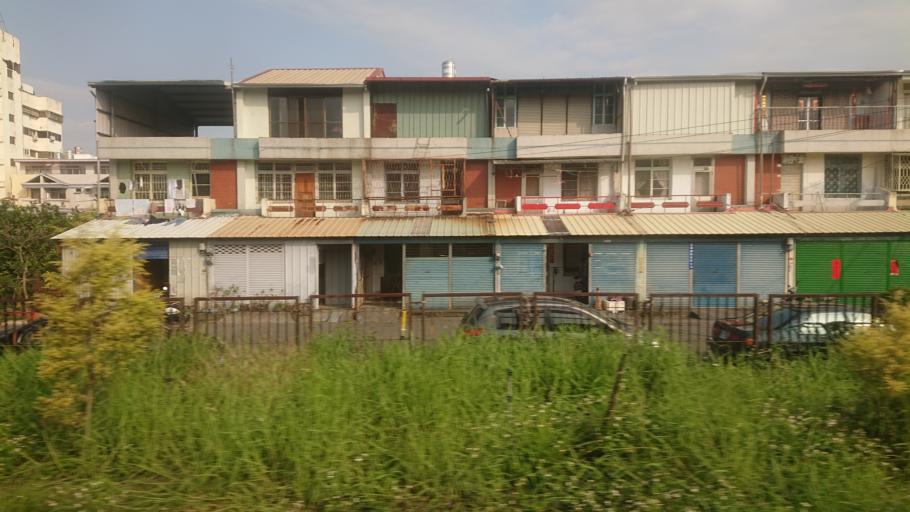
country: TW
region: Taiwan
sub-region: Yunlin
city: Douliu
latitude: 23.7146
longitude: 120.5501
